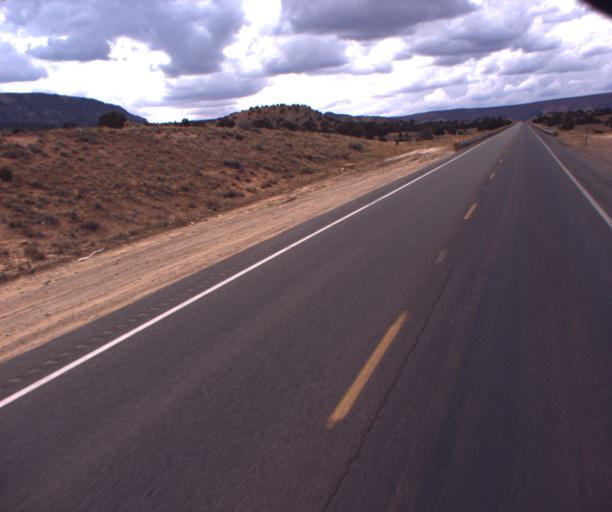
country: US
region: Arizona
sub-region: Navajo County
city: Kayenta
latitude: 36.6992
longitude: -110.3106
